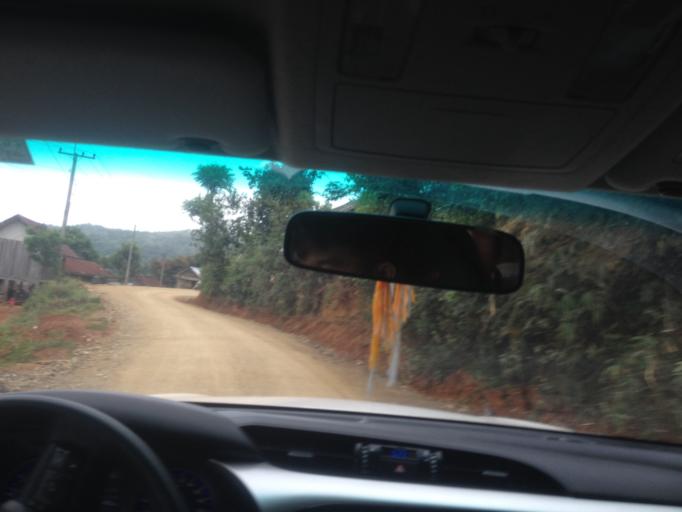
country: TH
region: Nan
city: Chaloem Phra Kiat
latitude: 19.9798
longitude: 101.1430
